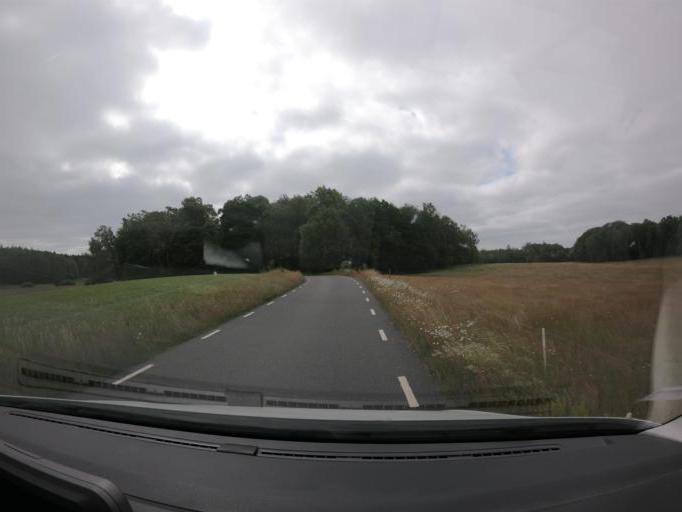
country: SE
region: Skane
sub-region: Eslovs Kommun
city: Stehag
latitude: 55.9844
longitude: 13.4276
